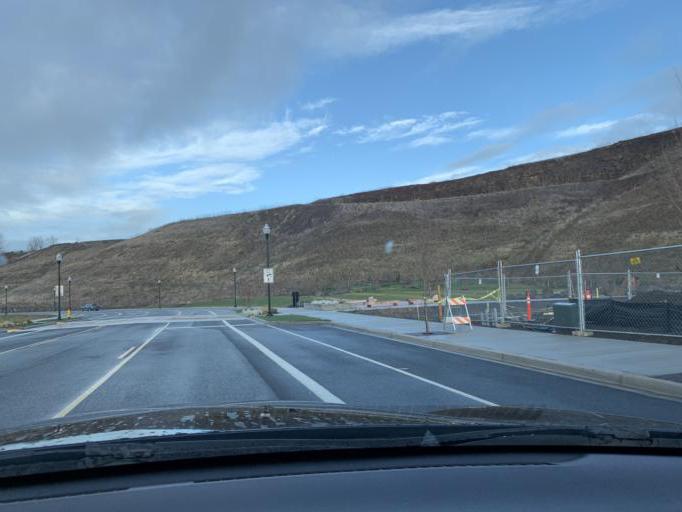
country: US
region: Washington
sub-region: Clark County
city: Mill Plain
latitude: 45.5886
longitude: -122.4704
